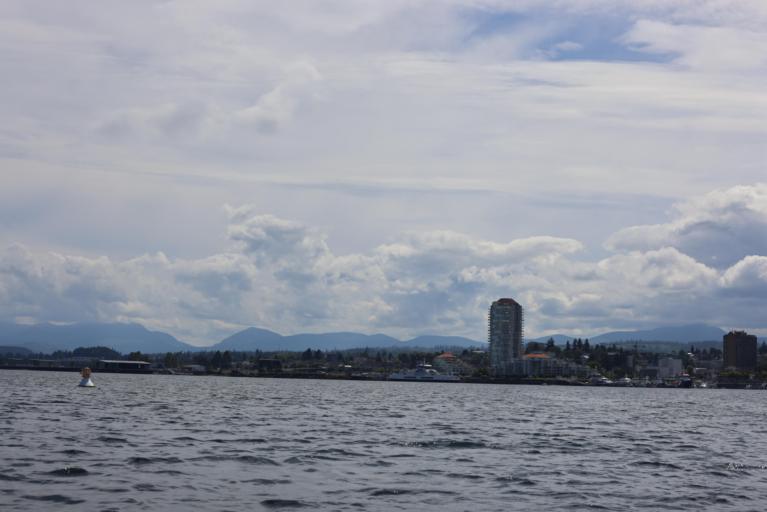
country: CA
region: British Columbia
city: Nanaimo
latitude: 49.1762
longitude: -123.9292
